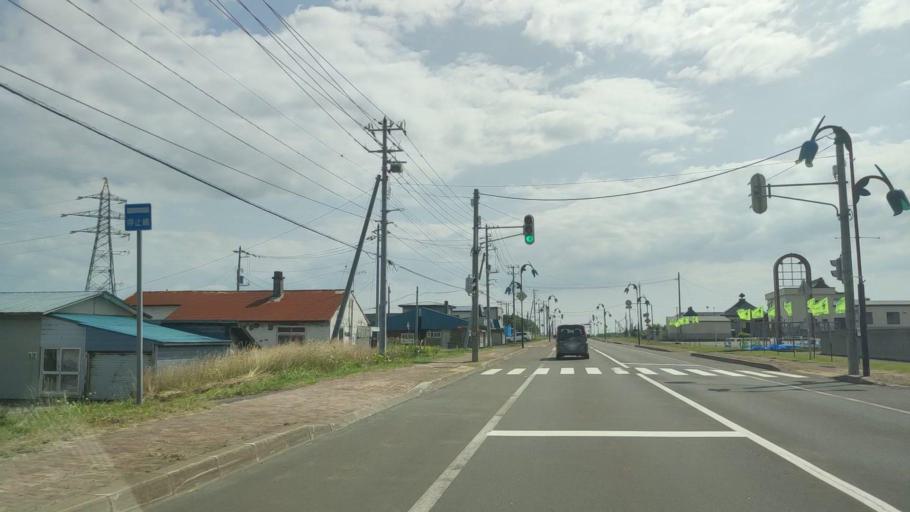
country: JP
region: Hokkaido
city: Rumoi
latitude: 44.3060
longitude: 141.6537
